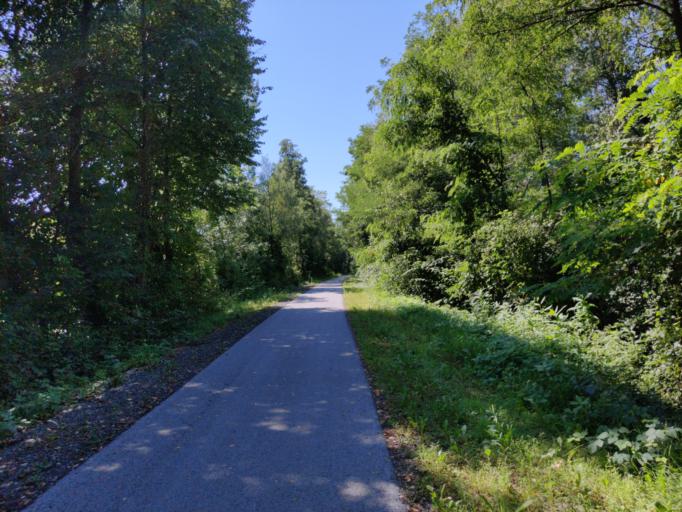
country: AT
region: Styria
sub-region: Politischer Bezirk Leibnitz
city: Stocking
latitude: 46.8712
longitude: 15.5317
